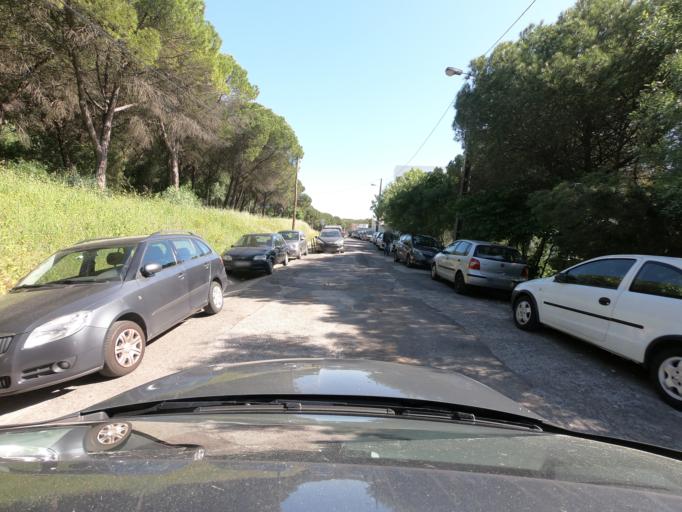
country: PT
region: Lisbon
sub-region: Oeiras
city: Alges
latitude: 38.7061
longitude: -9.2187
